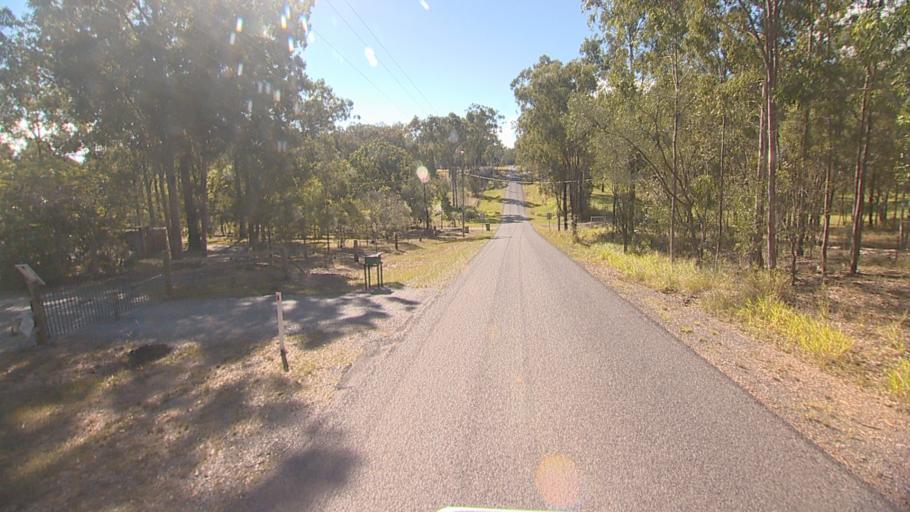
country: AU
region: Queensland
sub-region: Logan
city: Chambers Flat
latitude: -27.8118
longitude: 153.0782
